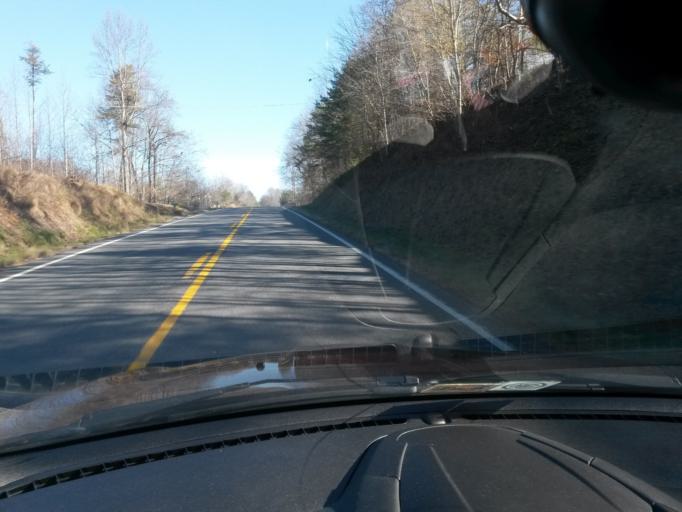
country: US
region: Virginia
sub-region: Patrick County
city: Patrick Springs
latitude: 36.7474
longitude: -80.2019
